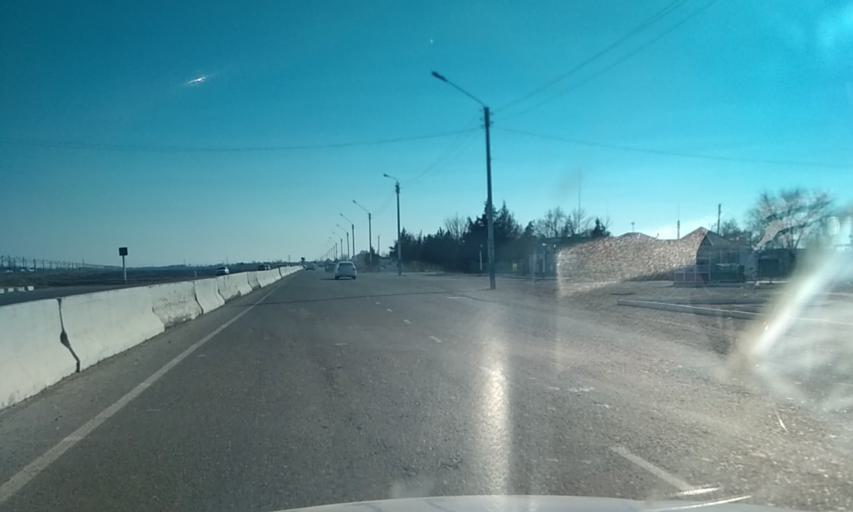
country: UZ
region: Sirdaryo
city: Guliston
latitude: 40.4695
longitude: 68.7719
